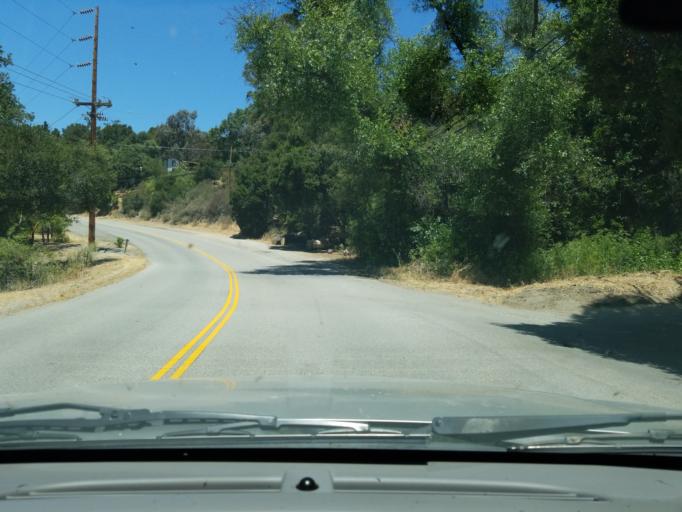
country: US
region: California
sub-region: Monterey County
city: Carmel Valley Village
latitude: 36.4754
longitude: -121.7188
